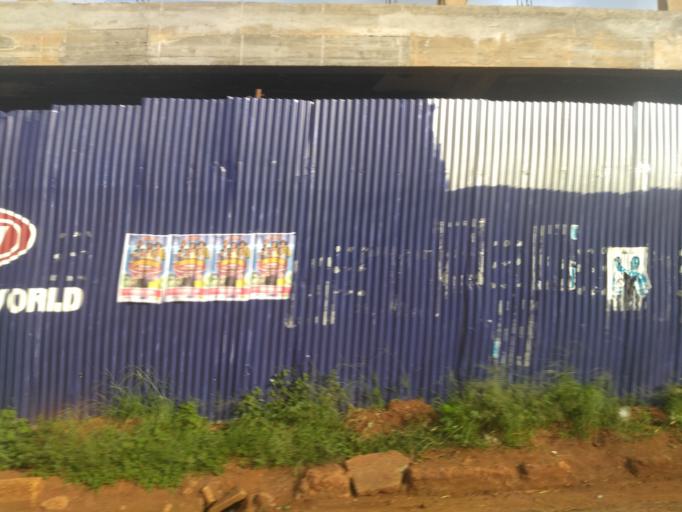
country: UG
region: Eastern Region
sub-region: Jinja District
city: Jinja
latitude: 0.4241
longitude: 33.2090
